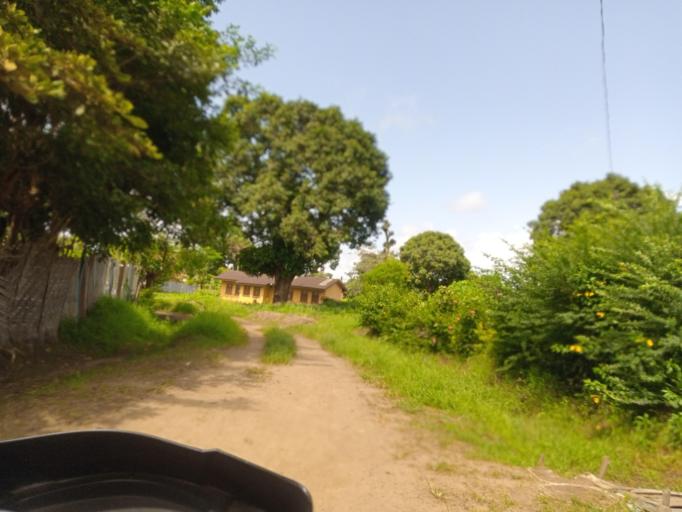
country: SL
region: Northern Province
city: Tintafor
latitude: 8.6246
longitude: -13.2099
